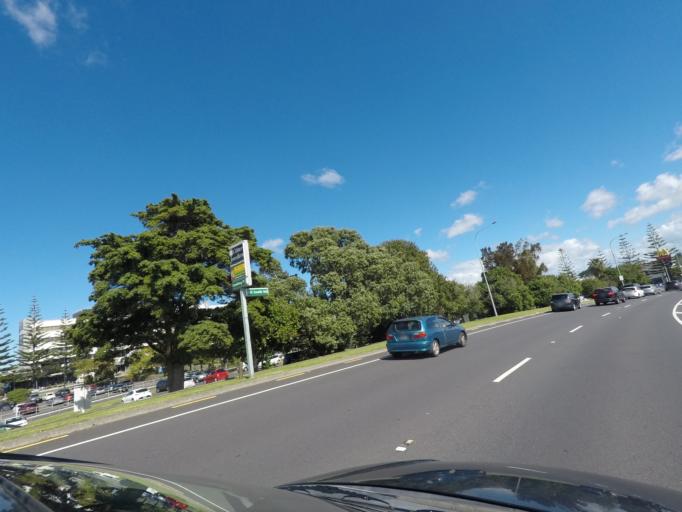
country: NZ
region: Auckland
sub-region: Auckland
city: Manukau City
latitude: -36.9908
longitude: 174.8838
